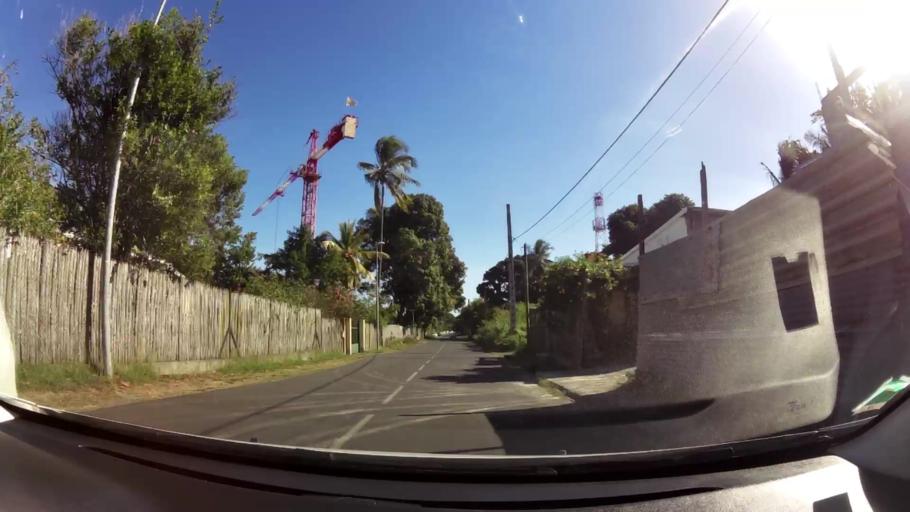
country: YT
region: Pamandzi
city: Pamandzi
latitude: -12.7949
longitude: 45.2774
